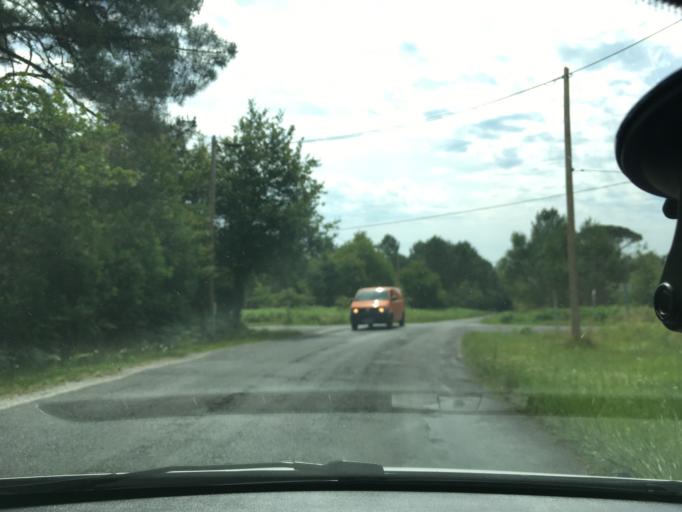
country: FR
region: Aquitaine
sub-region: Departement de la Gironde
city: Gaillan-en-Medoc
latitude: 45.3409
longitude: -1.0086
